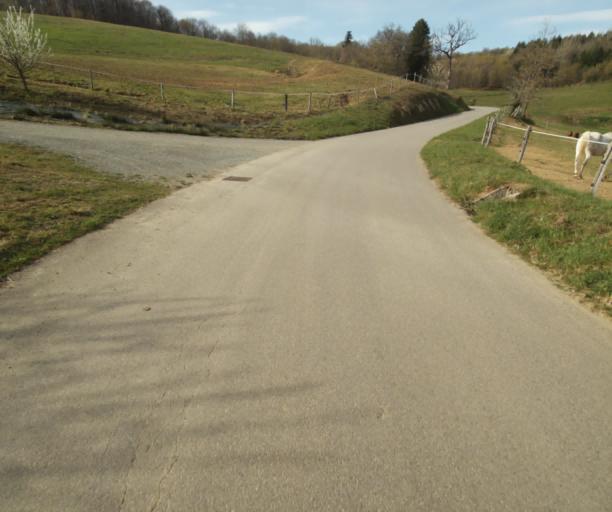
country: FR
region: Limousin
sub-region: Departement de la Correze
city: Naves
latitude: 45.3220
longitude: 1.7252
